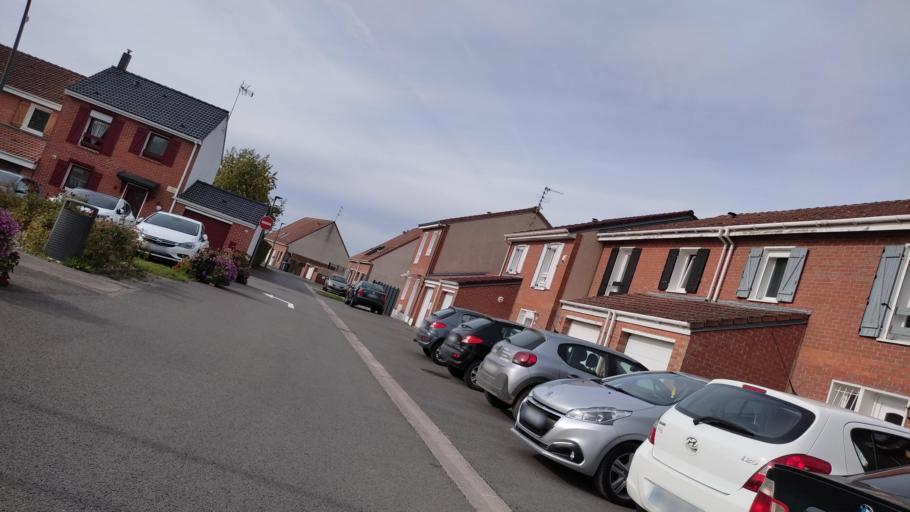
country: FR
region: Nord-Pas-de-Calais
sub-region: Departement du Pas-de-Calais
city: Feuchy
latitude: 50.3058
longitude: 2.8374
